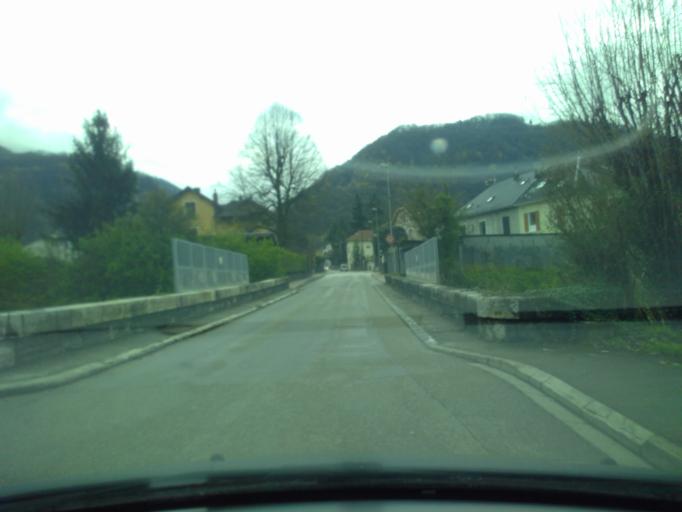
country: FR
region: Rhone-Alpes
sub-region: Departement de l'Isere
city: Domene
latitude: 45.2057
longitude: 5.8352
